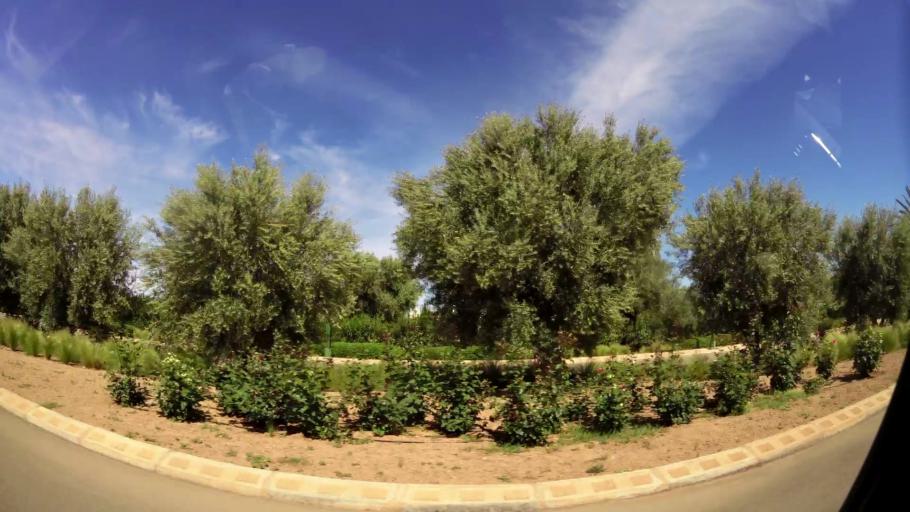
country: MA
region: Marrakech-Tensift-Al Haouz
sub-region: Marrakech
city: Marrakesh
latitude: 31.6172
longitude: -7.9491
